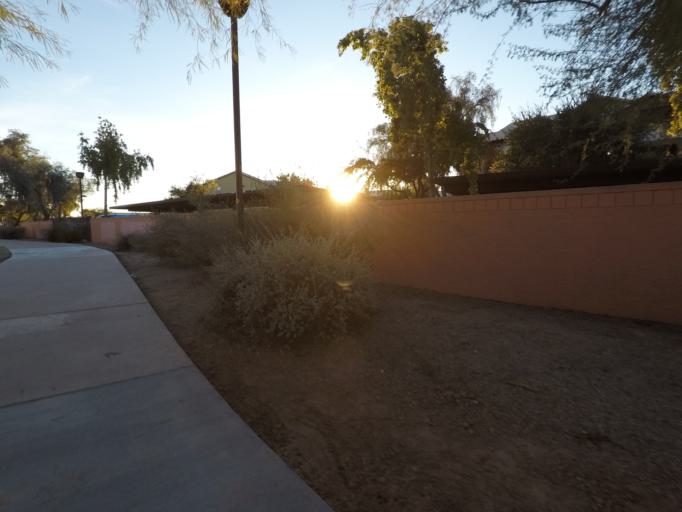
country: US
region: Arizona
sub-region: Maricopa County
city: Guadalupe
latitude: 33.3527
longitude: -111.9577
